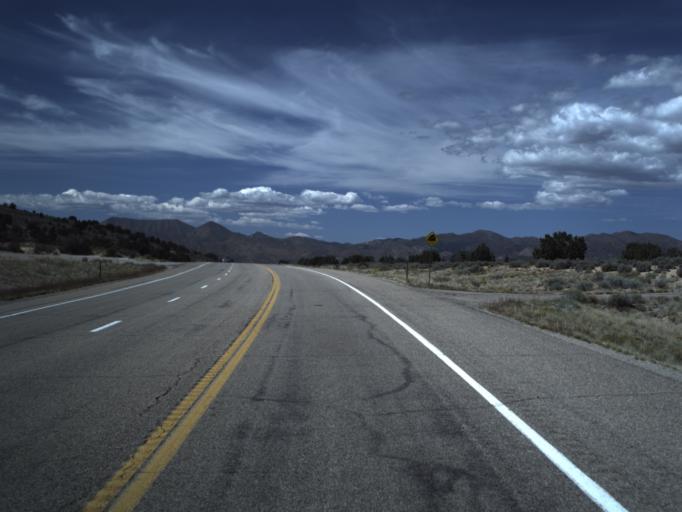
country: US
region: Utah
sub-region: Washington County
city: Ivins
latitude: 37.3192
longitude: -113.6829
